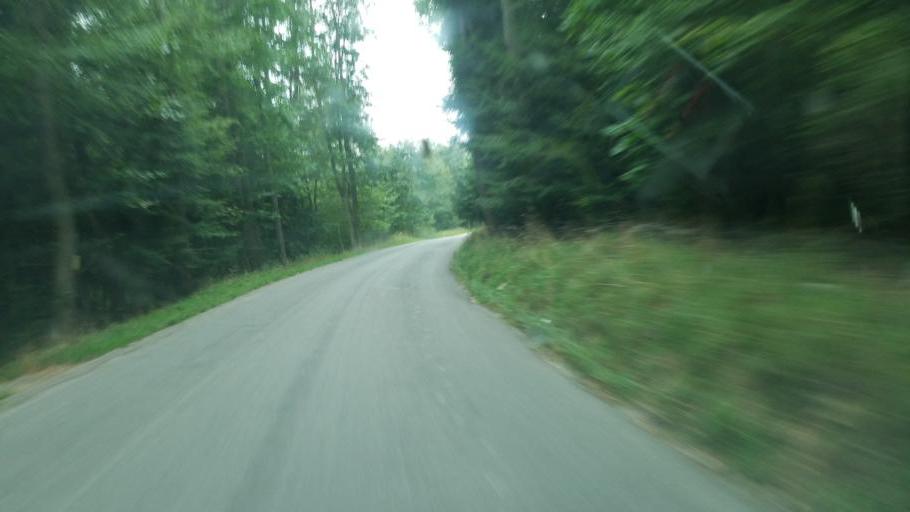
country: US
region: Pennsylvania
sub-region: Clarion County
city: Knox
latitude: 41.1689
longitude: -79.5288
